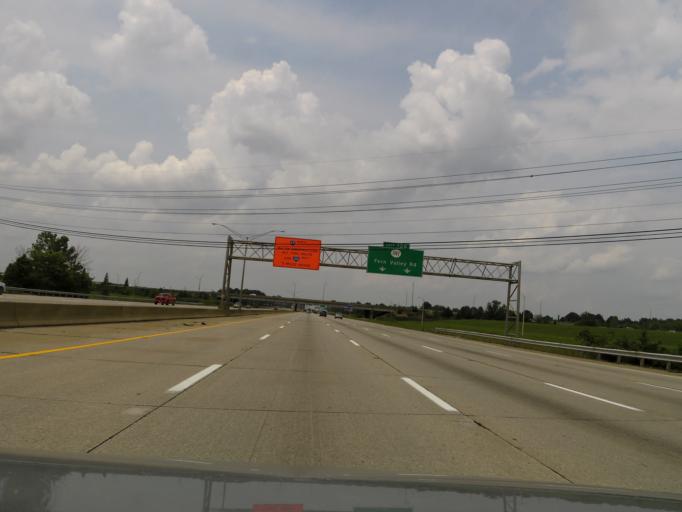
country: US
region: Kentucky
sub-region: Jefferson County
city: Heritage Creek
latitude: 38.1342
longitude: -85.7052
